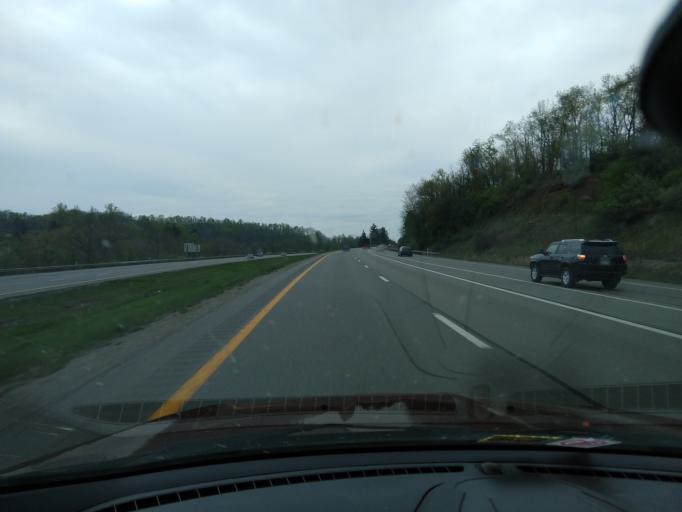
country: US
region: West Virginia
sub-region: Lewis County
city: Weston
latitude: 39.1073
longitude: -80.3919
